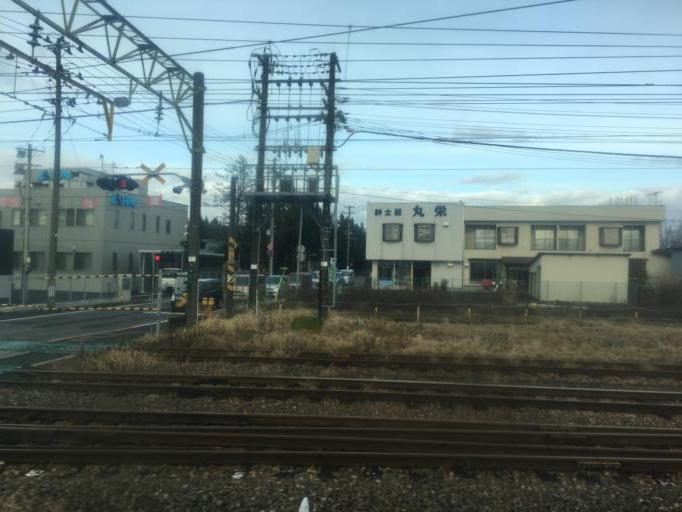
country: JP
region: Akita
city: Odate
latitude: 40.2889
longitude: 140.5598
